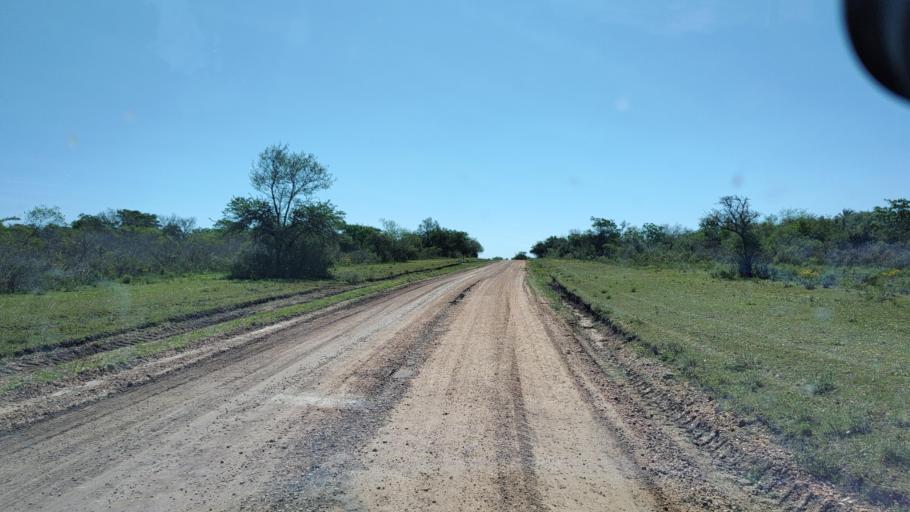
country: AR
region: Entre Rios
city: Ubajay
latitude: -31.8719
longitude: -58.2390
